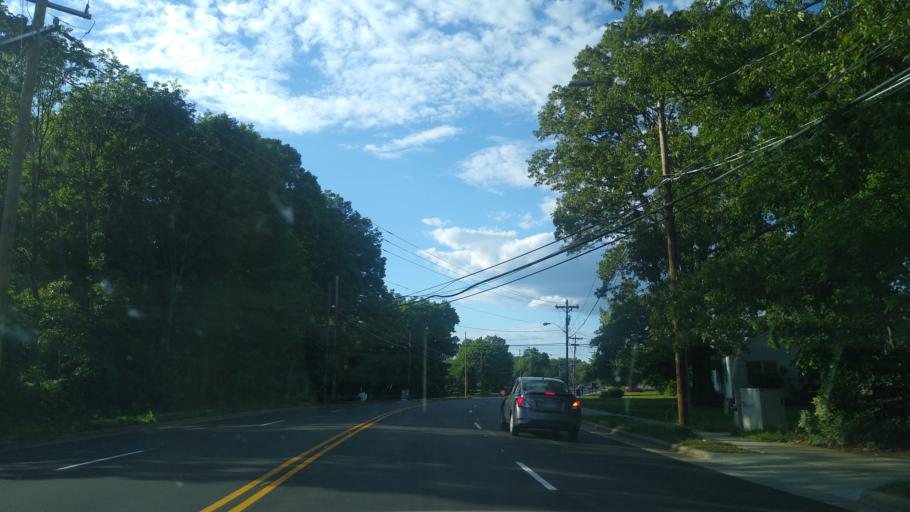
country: US
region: North Carolina
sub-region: Guilford County
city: Greensboro
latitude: 36.1284
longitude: -79.7745
